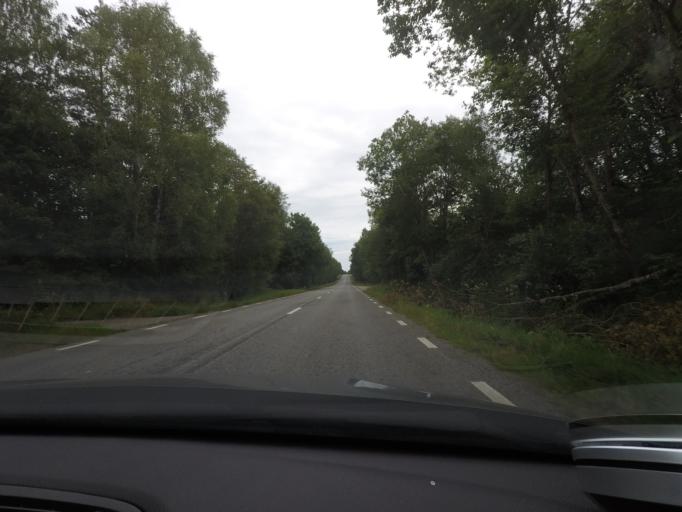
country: SE
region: Blekinge
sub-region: Olofstroms Kommun
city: Olofstroem
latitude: 56.4638
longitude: 14.6195
